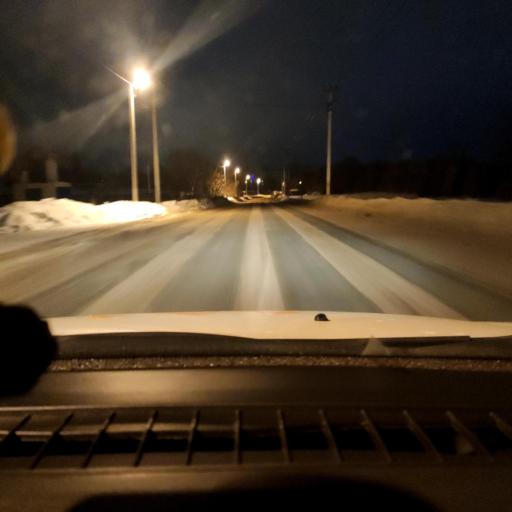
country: RU
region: Samara
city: Chapayevsk
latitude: 52.9893
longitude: 49.7267
